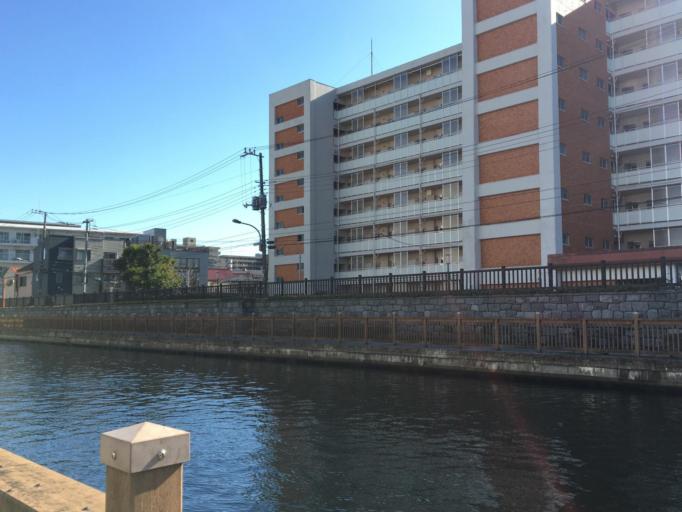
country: JP
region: Tokyo
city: Urayasu
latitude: 35.6858
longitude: 139.8370
